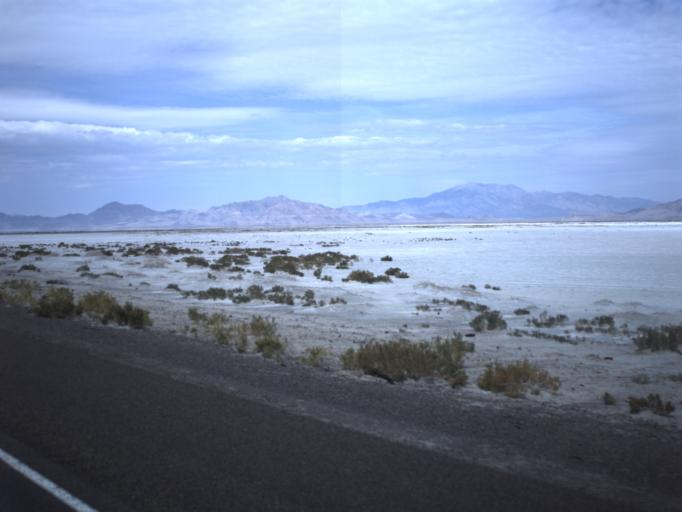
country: US
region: Utah
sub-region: Tooele County
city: Wendover
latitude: 40.7368
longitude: -113.7261
